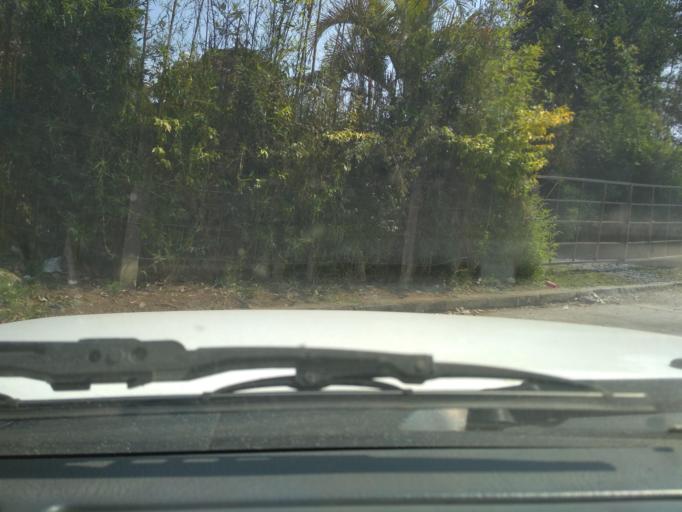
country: MX
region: Veracruz
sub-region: Mariano Escobedo
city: Palmira
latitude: 18.8741
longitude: -97.0961
